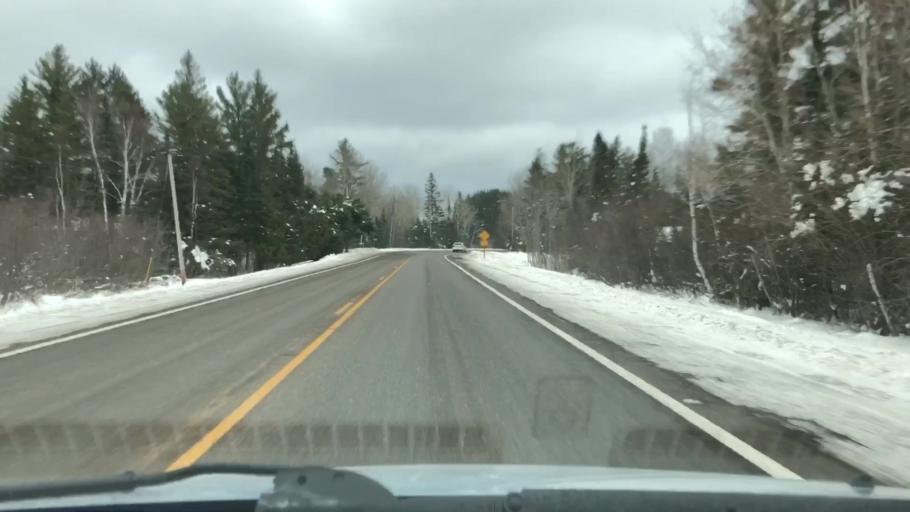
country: US
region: Minnesota
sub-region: Carlton County
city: Esko
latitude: 46.6862
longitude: -92.3648
